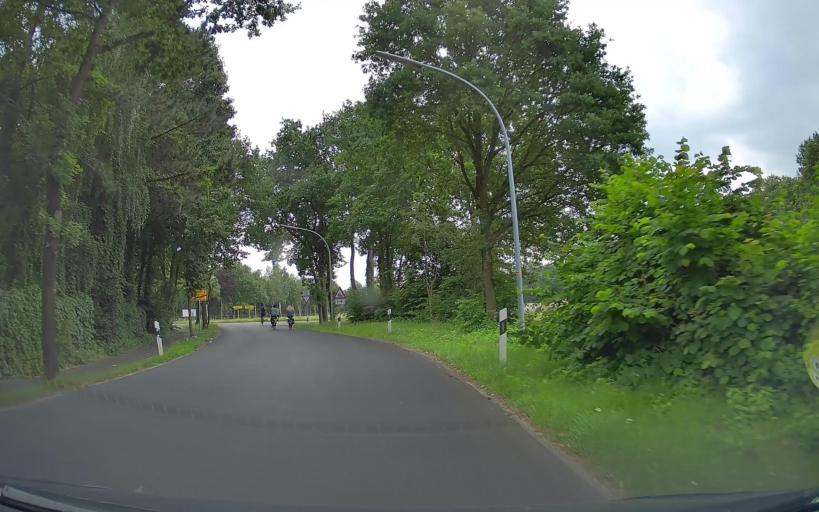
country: DE
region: Lower Saxony
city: Bosel
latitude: 52.9974
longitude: 7.9521
